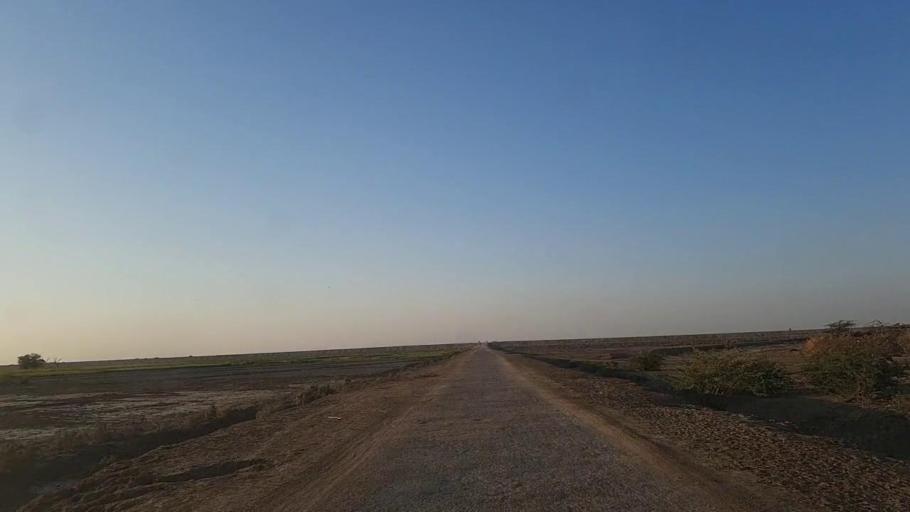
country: PK
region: Sindh
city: Naukot
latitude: 25.0027
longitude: 69.4208
